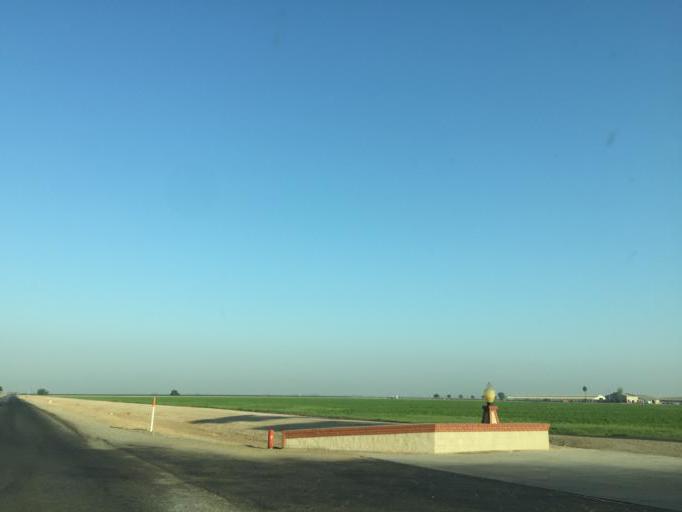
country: US
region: California
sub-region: Tulare County
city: Cutler
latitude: 36.4580
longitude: -119.3405
